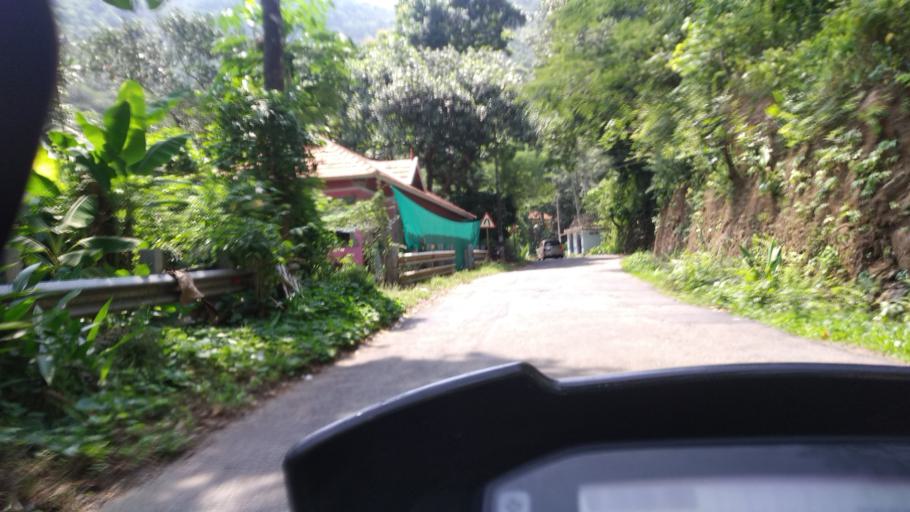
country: IN
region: Kerala
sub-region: Kottayam
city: Erattupetta
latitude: 9.6927
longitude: 76.8705
